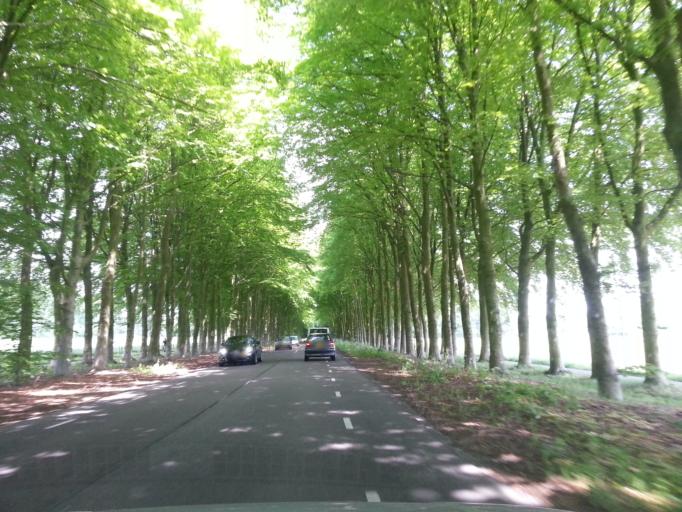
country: NL
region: Gelderland
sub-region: Gemeente Rheden
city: De Steeg
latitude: 52.0263
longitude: 6.0743
